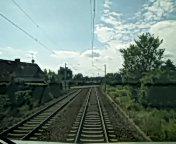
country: DE
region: Brandenburg
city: Halbe
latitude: 52.0764
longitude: 13.7269
